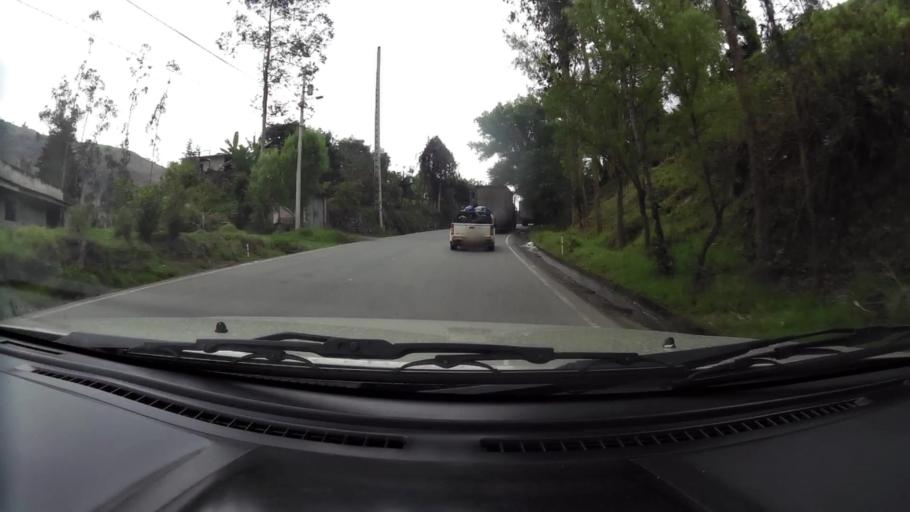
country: EC
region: Chimborazo
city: Alausi
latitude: -2.3118
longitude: -78.9072
